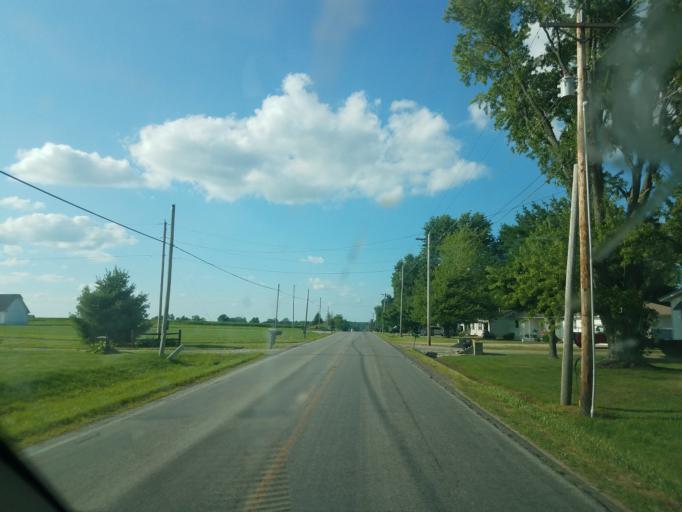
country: US
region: Ohio
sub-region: Wayne County
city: Apple Creek
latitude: 40.7429
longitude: -81.8961
